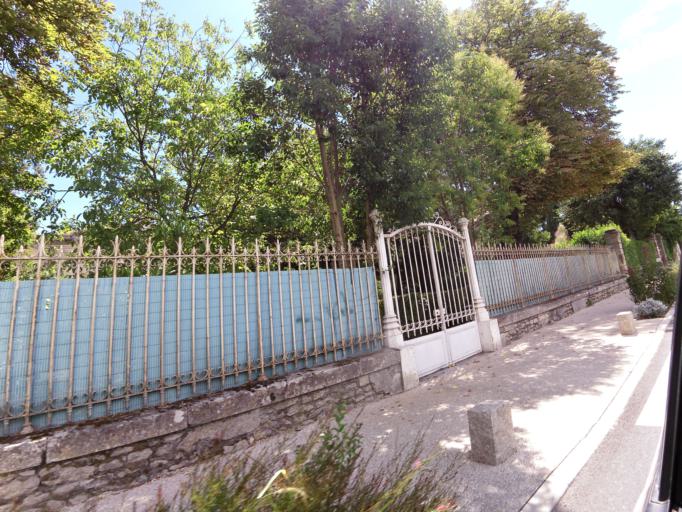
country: FR
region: Languedoc-Roussillon
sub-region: Departement du Gard
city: Sommieres
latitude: 43.7885
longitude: 4.0902
